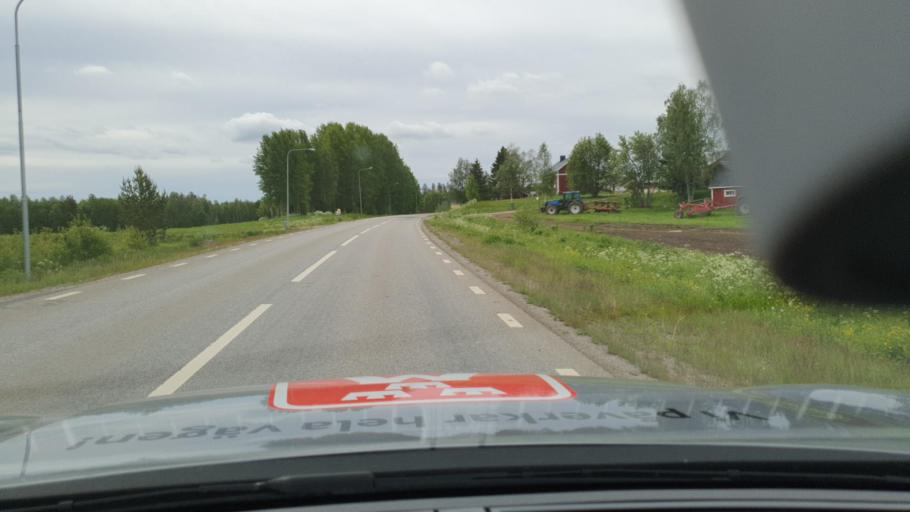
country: SE
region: Norrbotten
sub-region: Kalix Kommun
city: Kalix
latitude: 65.9709
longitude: 23.4609
